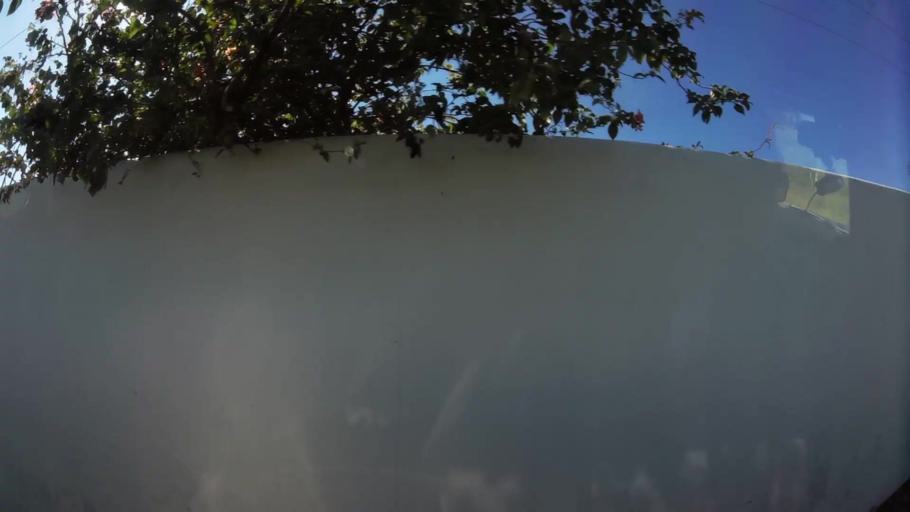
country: GT
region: Santa Rosa
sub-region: Municipio de Taxisco
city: Taxisco
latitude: 13.8808
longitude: -90.4537
